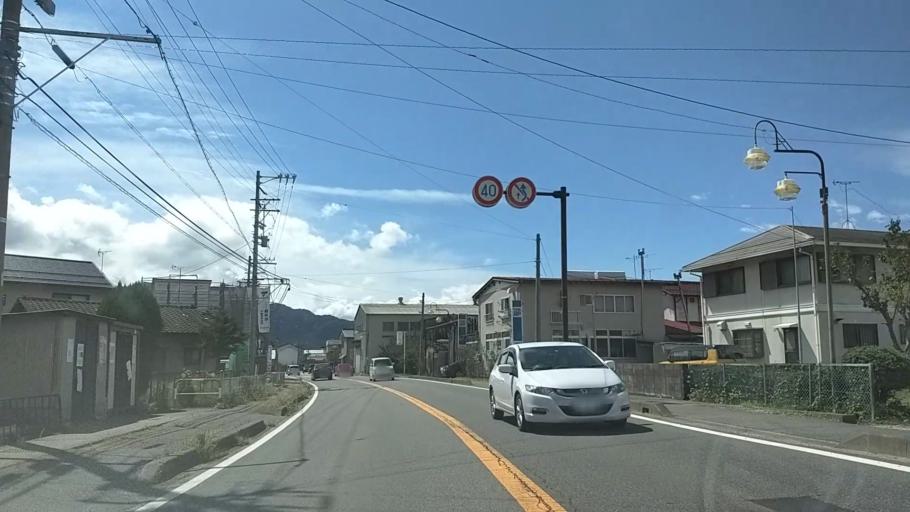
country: JP
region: Nagano
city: Suzaka
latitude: 36.6282
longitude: 138.2604
